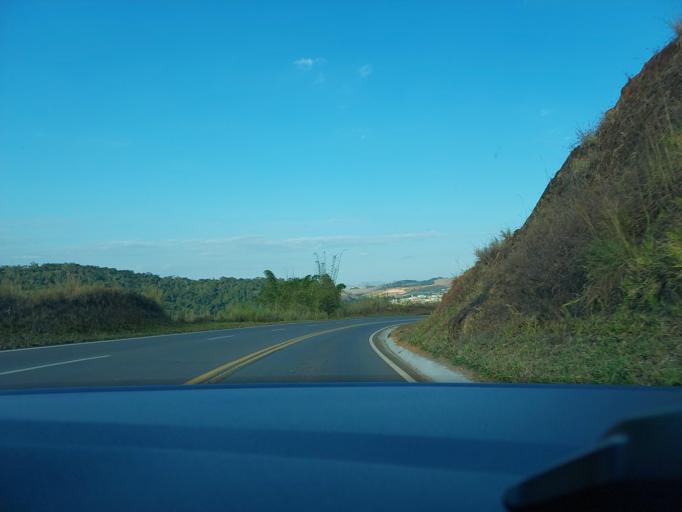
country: BR
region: Minas Gerais
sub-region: Muriae
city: Muriae
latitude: -21.0969
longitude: -42.4678
